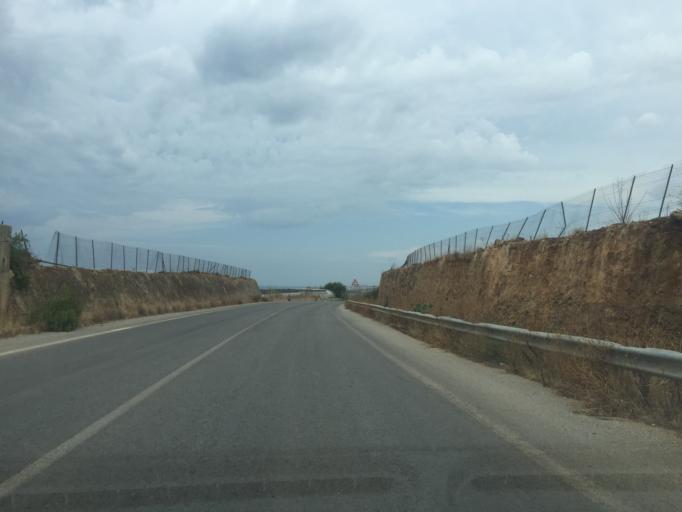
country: IT
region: Sicily
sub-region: Ragusa
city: Donnalucata
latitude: 36.7726
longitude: 14.6236
